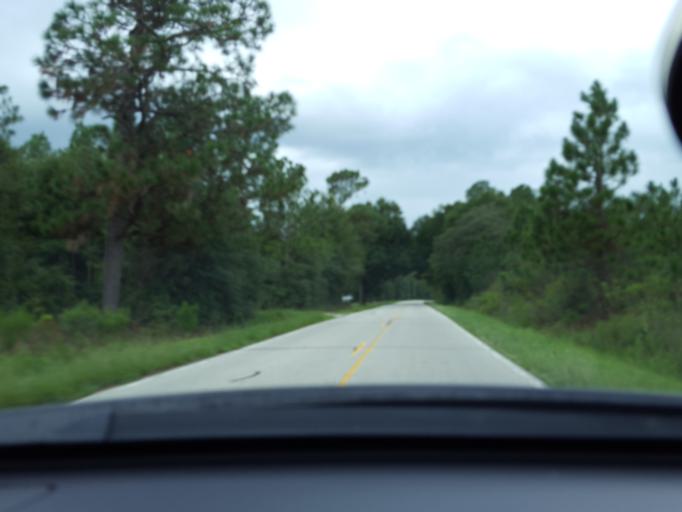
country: US
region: North Carolina
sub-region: Sampson County
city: Clinton
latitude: 34.7998
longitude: -78.2685
